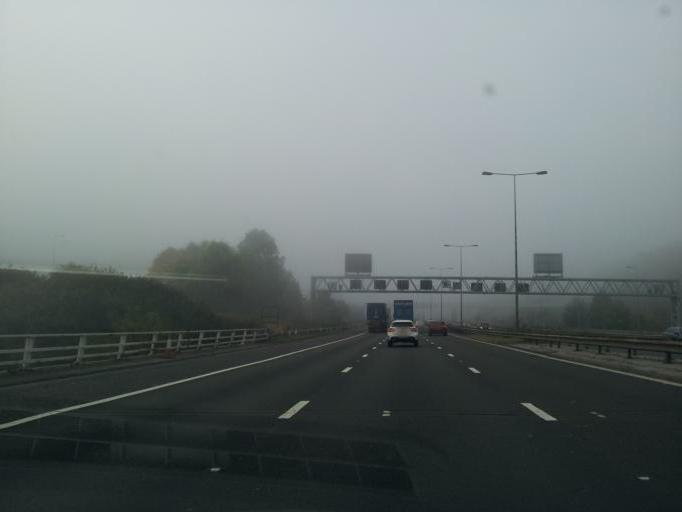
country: GB
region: England
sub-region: Kirklees
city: Cleckheaton
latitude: 53.7358
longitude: -1.7269
